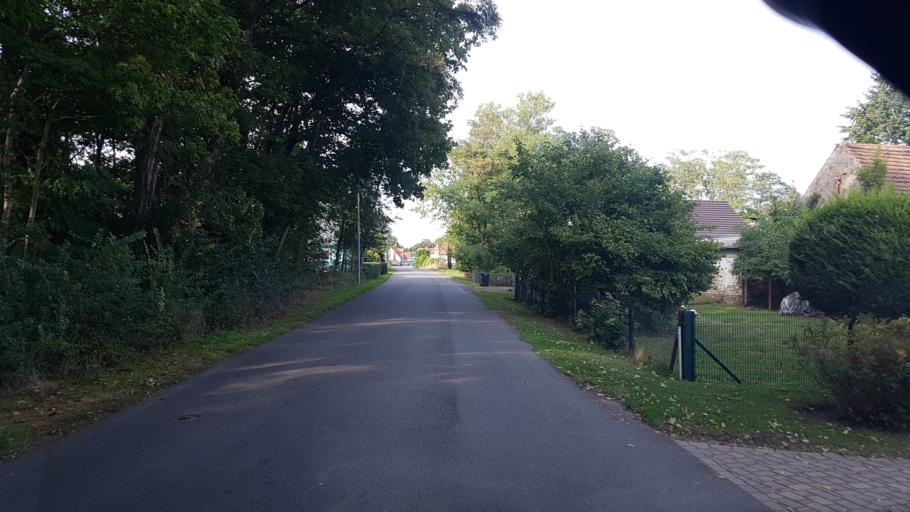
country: DE
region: Brandenburg
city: Welzow
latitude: 51.5766
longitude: 14.1103
